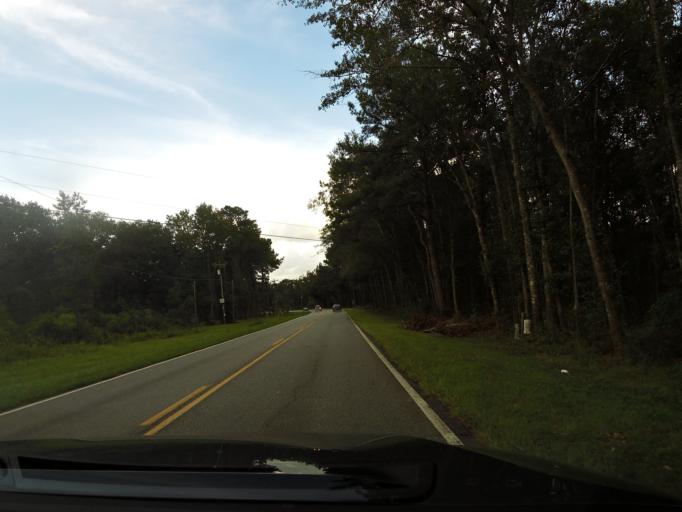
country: US
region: Georgia
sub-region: Liberty County
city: Midway
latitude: 31.8447
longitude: -81.4159
